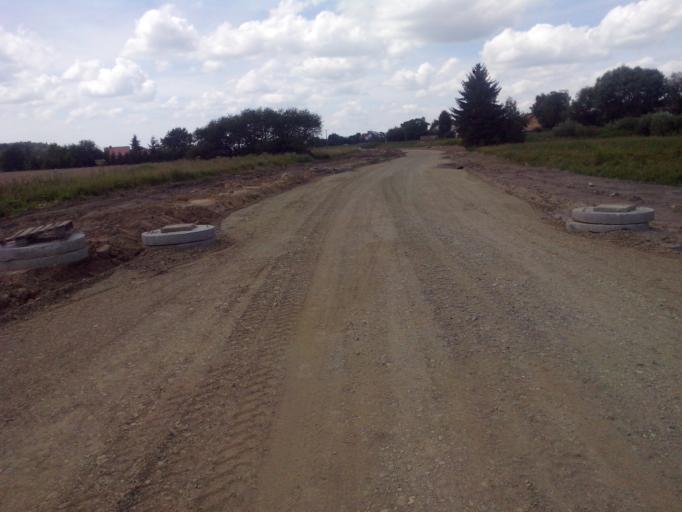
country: PL
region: Subcarpathian Voivodeship
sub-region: Powiat strzyzowski
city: Strzyzow
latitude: 49.8680
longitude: 21.7787
